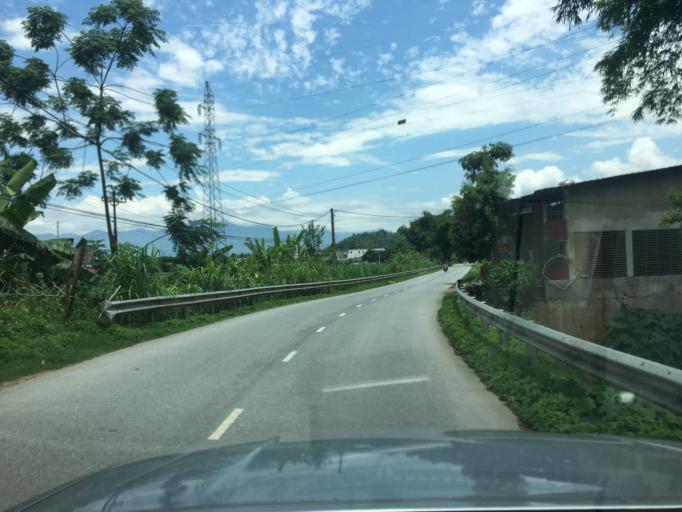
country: VN
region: Yen Bai
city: Son Thinh
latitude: 21.6466
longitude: 104.5011
